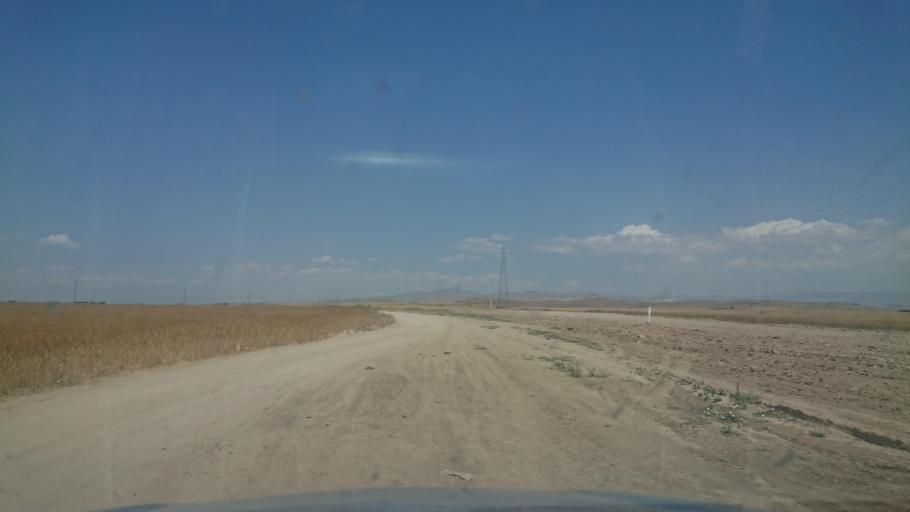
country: TR
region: Aksaray
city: Sariyahsi
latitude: 39.0016
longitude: 33.8891
